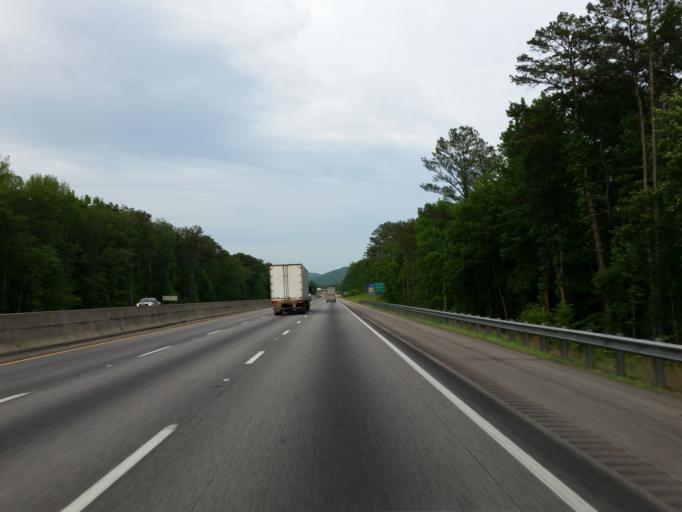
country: US
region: Alabama
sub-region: Saint Clair County
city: Moody
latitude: 33.5731
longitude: -86.4902
